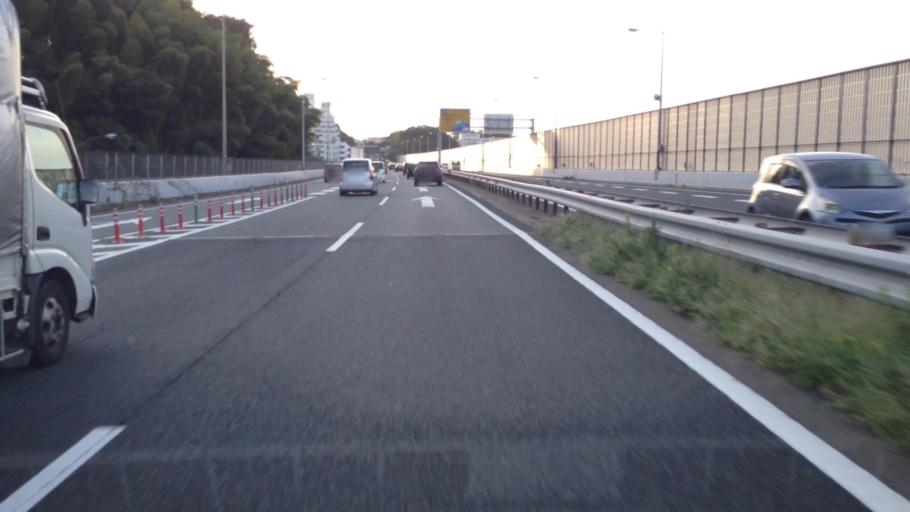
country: JP
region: Kanagawa
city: Kamakura
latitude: 35.3839
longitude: 139.5826
